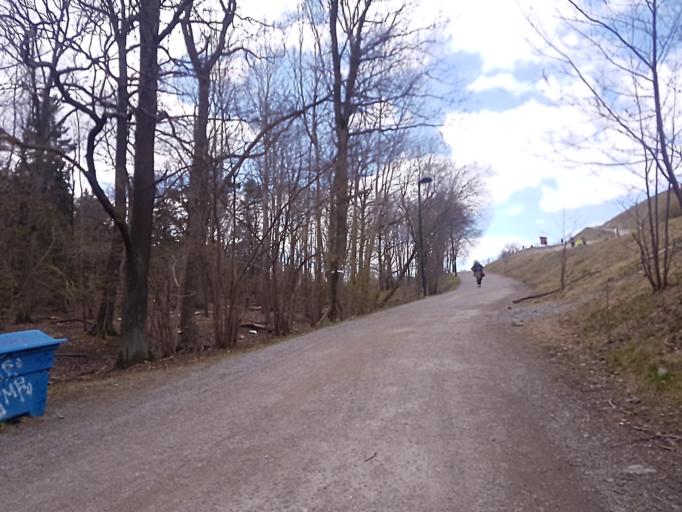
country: SE
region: Stockholm
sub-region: Stockholms Kommun
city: OEstermalm
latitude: 59.3003
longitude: 18.1146
